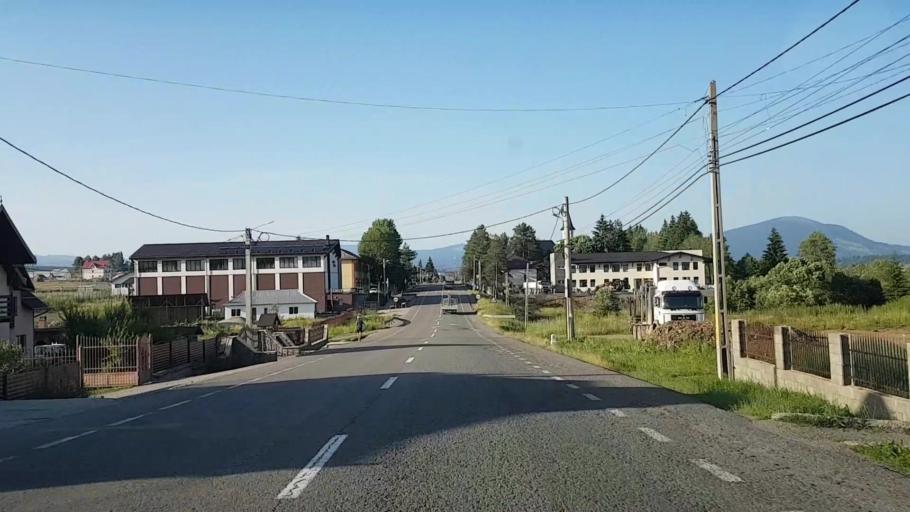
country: RO
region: Suceava
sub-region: Comuna Poiana Stampei
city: Poiana Stampei
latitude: 47.3183
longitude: 25.1350
